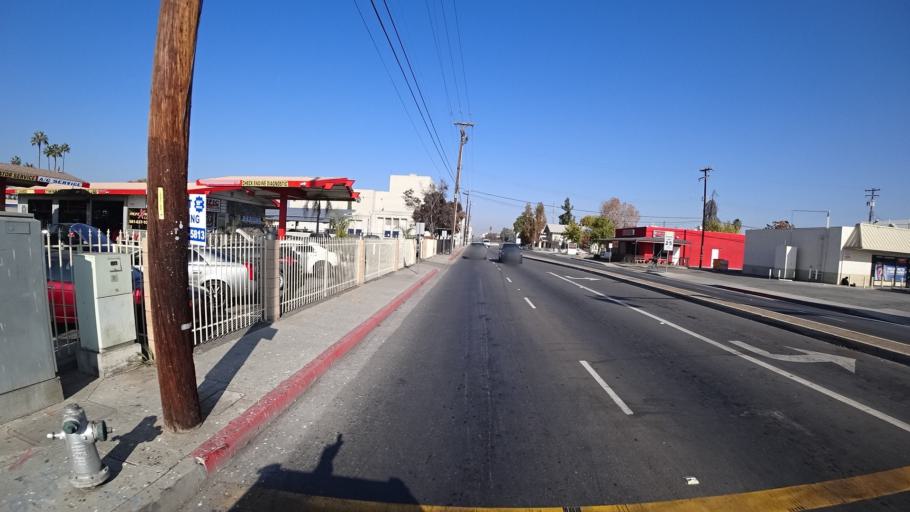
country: US
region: California
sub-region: Kern County
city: Bakersfield
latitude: 35.3687
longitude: -119.0213
